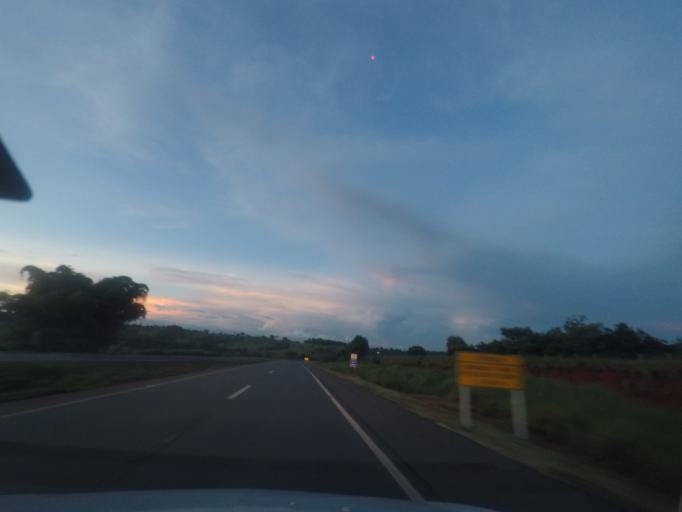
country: BR
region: Goias
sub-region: Pontalina
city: Pontalina
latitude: -17.5004
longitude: -49.2149
